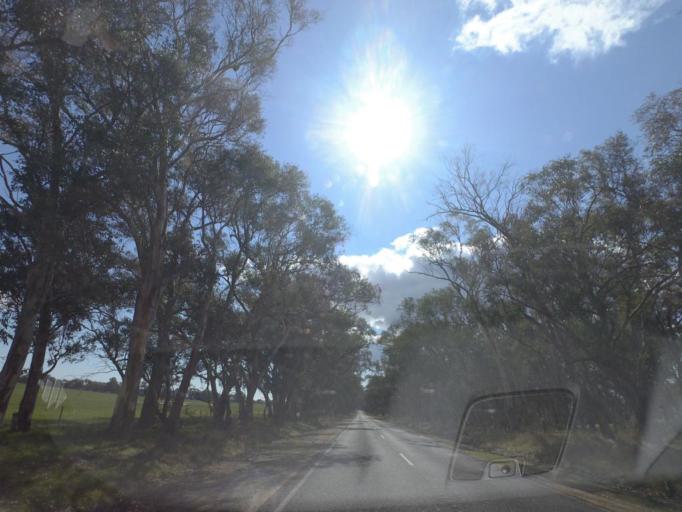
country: AU
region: New South Wales
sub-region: Corowa Shire
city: Howlong
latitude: -36.2268
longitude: 146.6295
